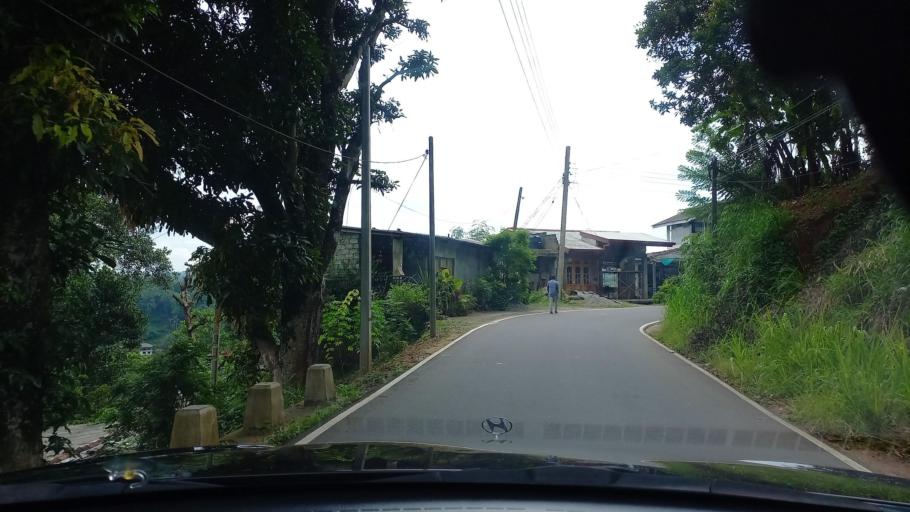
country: LK
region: Central
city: Gampola
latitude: 7.2261
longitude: 80.6055
